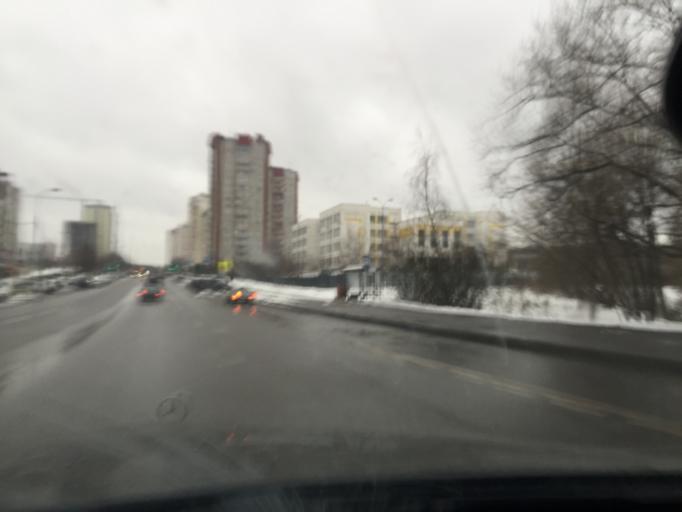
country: RU
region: Moscow
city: Troparevo
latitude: 55.6546
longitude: 37.4710
